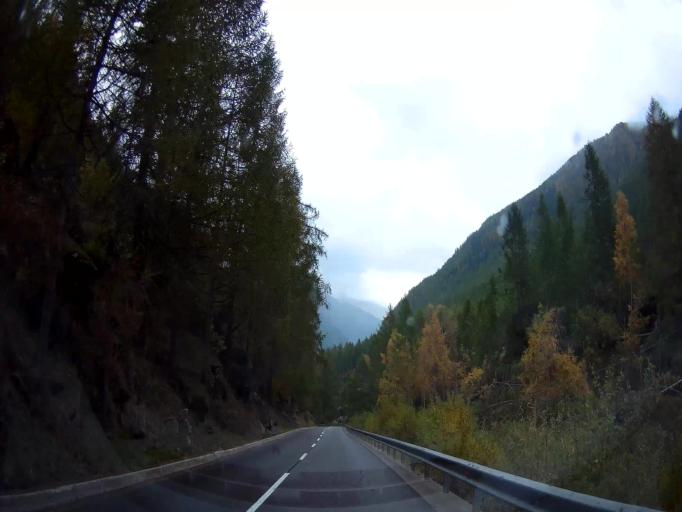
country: IT
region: Trentino-Alto Adige
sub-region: Bolzano
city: Senales
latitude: 46.7154
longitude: 10.8738
